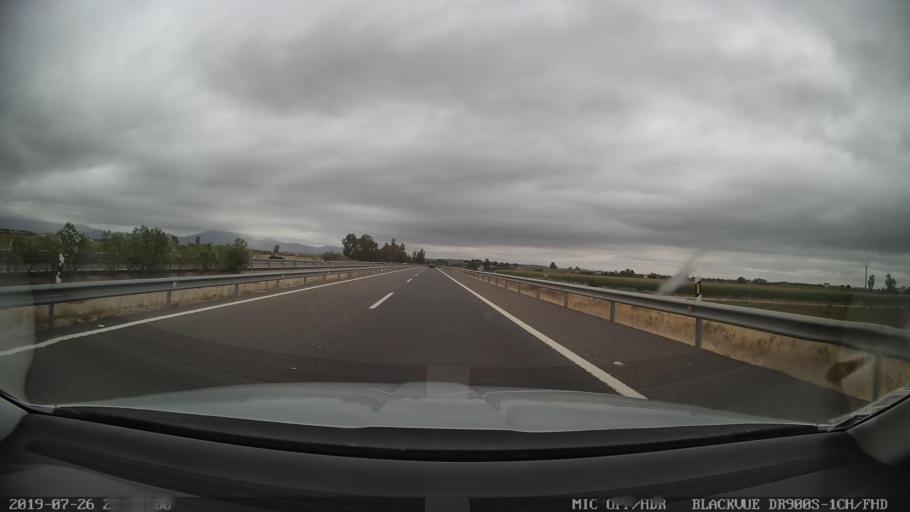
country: ES
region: Extremadura
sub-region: Provincia de Badajoz
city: Santa Amalia
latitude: 39.0888
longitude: -6.0189
